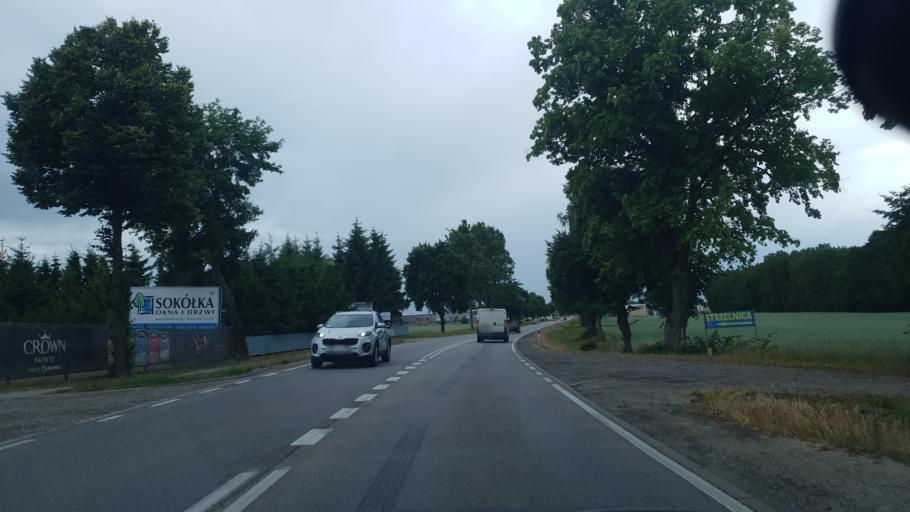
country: PL
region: Pomeranian Voivodeship
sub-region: Powiat kartuski
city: Banino
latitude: 54.4095
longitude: 18.3696
